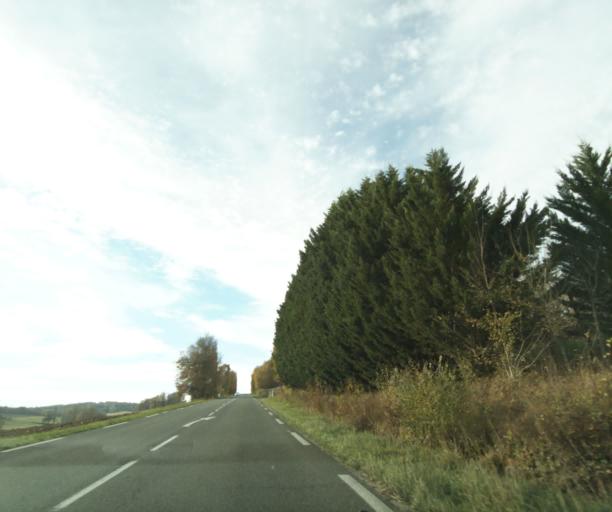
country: FR
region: Midi-Pyrenees
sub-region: Departement du Gers
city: Vic-Fezensac
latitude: 43.7578
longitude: 0.2233
